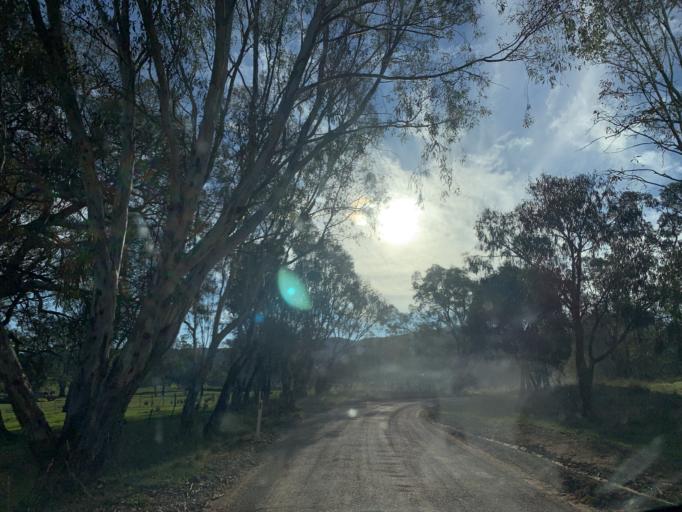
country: AU
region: Victoria
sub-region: Mansfield
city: Mansfield
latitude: -36.9591
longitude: 146.1022
